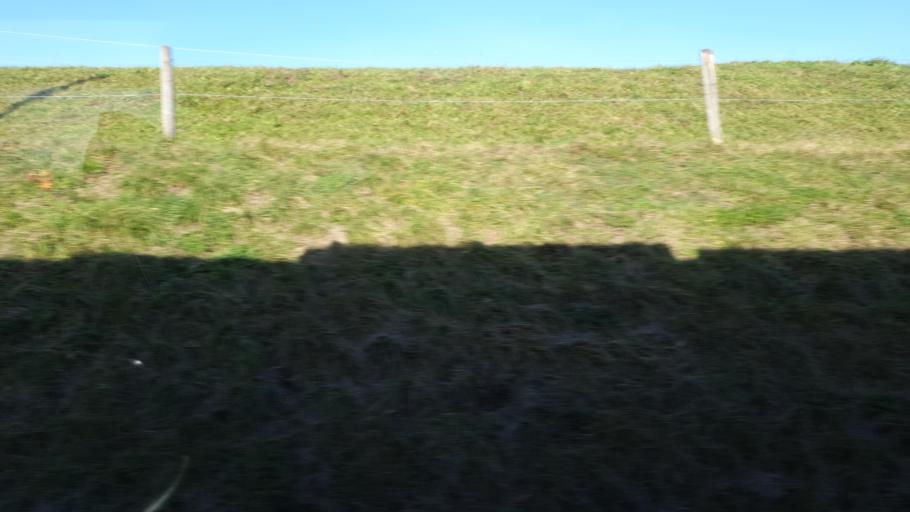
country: CH
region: Fribourg
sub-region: Gruyere District
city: Vuadens
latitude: 46.6175
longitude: 6.9950
